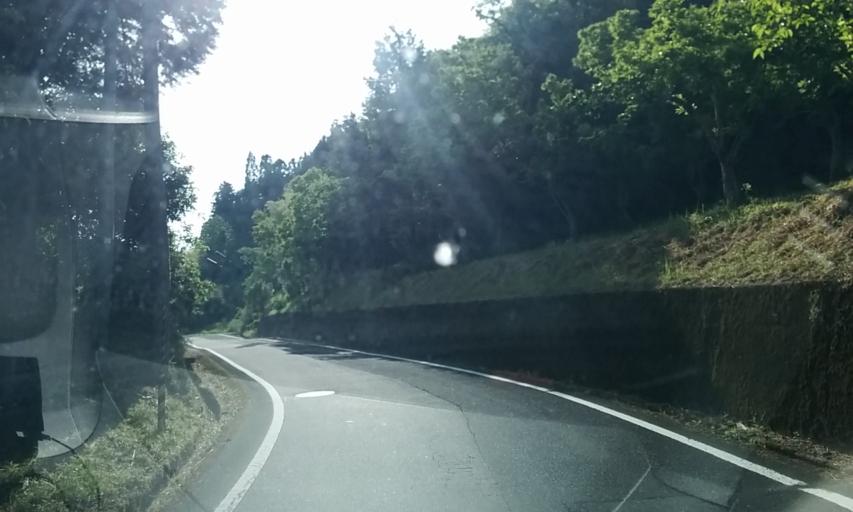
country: JP
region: Kyoto
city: Ayabe
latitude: 35.3361
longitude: 135.3010
